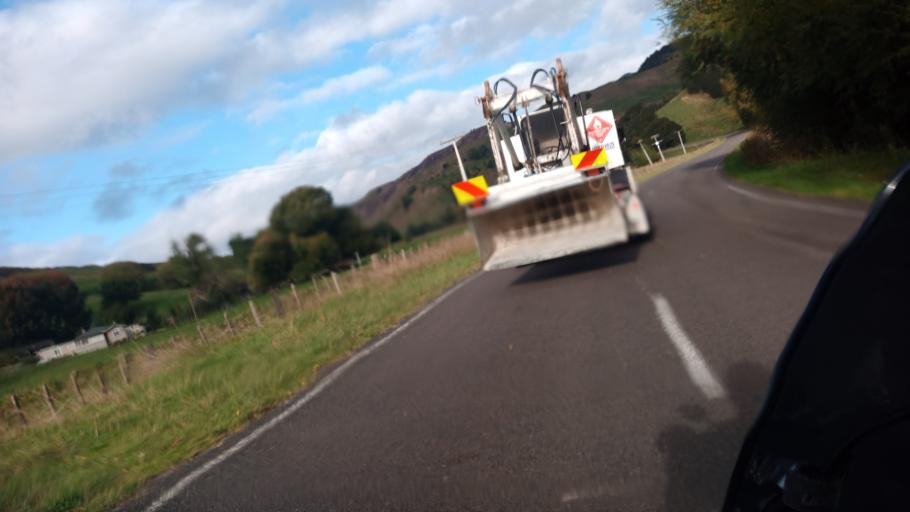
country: NZ
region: Gisborne
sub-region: Gisborne District
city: Gisborne
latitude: -38.5898
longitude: 177.7826
